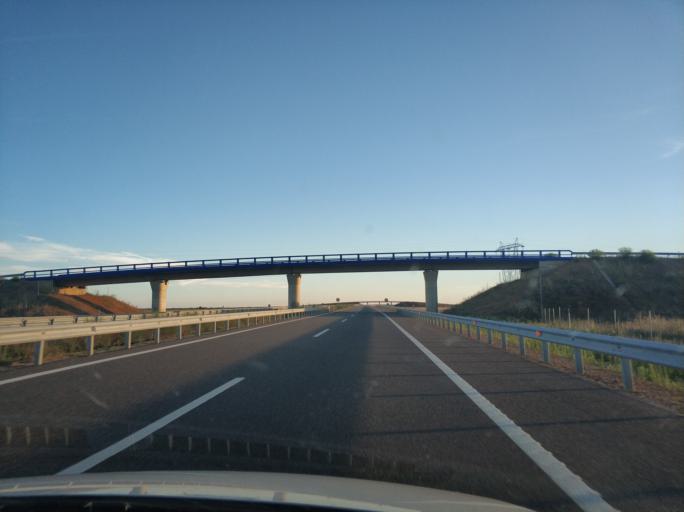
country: ES
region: Castille and Leon
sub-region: Provincia de Zamora
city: Barcial del Barco
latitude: 41.9400
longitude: -5.6401
